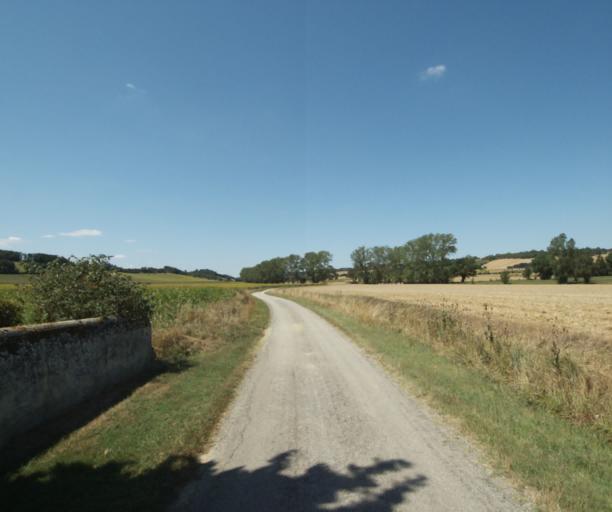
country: FR
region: Midi-Pyrenees
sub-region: Departement de la Haute-Garonne
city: Saint-Felix-Lauragais
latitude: 43.4875
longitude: 1.8733
